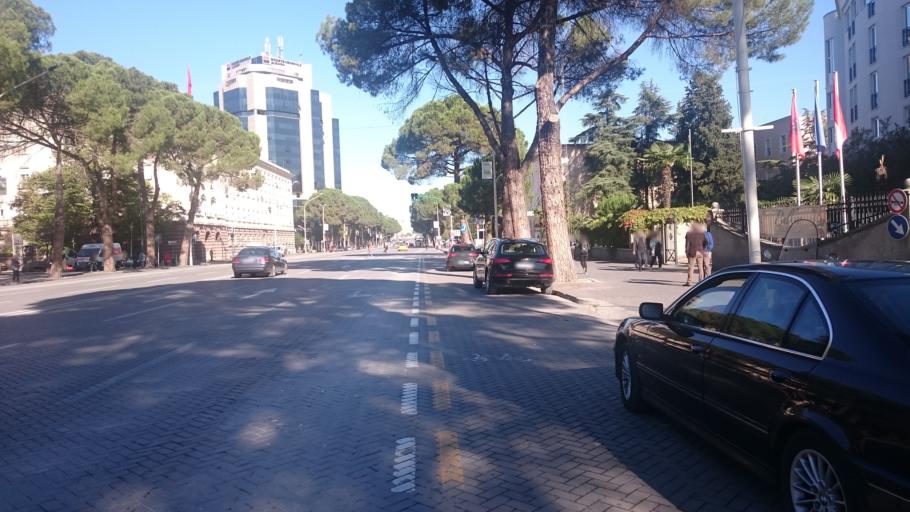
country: AL
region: Tirane
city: Tirana
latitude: 41.3205
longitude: 19.8207
